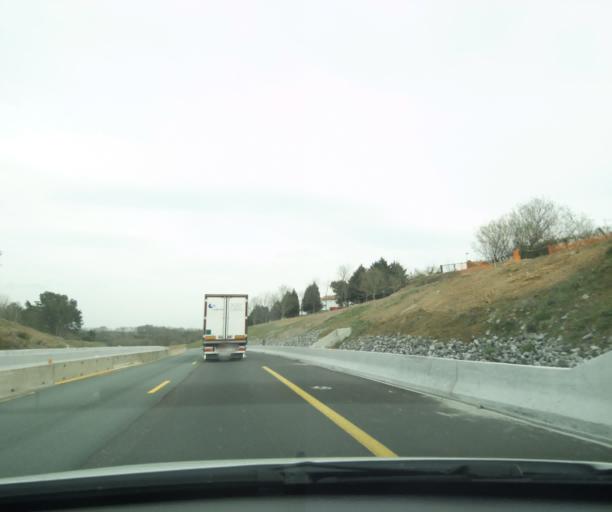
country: FR
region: Aquitaine
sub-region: Departement des Pyrenees-Atlantiques
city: Saint-Jean-de-Luz
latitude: 43.3736
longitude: -1.6588
